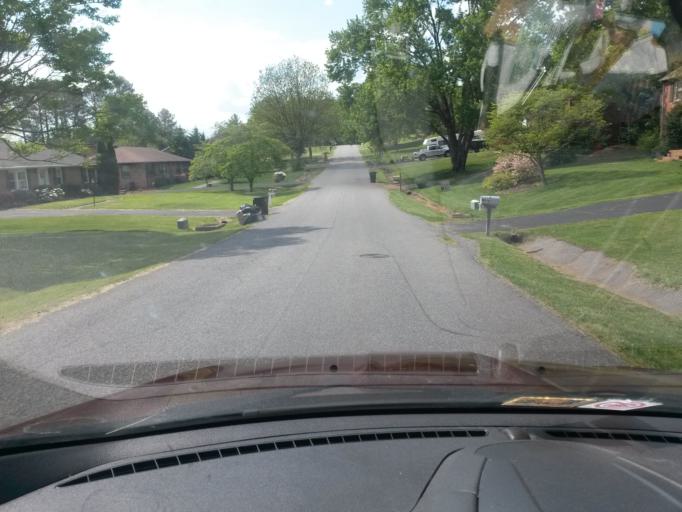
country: US
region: Virginia
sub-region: Campbell County
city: Timberlake
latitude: 37.3469
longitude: -79.2176
